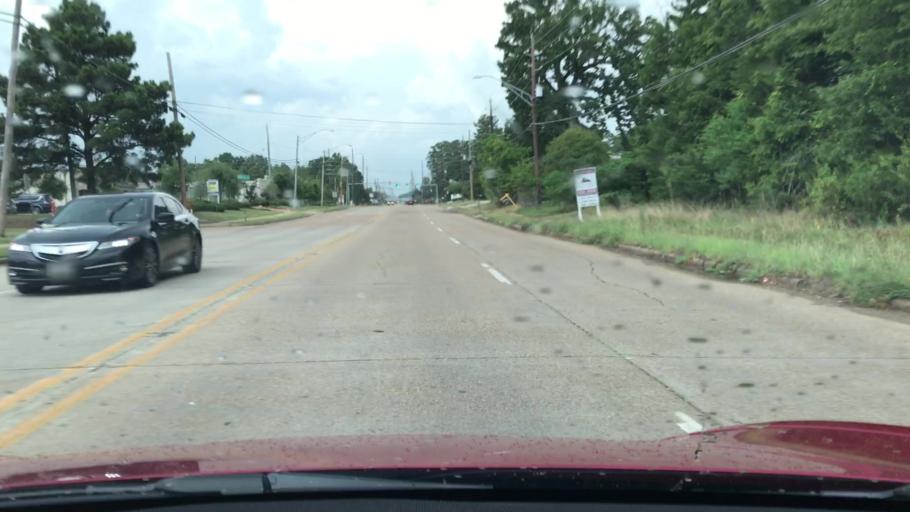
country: US
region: Louisiana
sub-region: Bossier Parish
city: Bossier City
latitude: 32.4107
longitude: -93.7632
